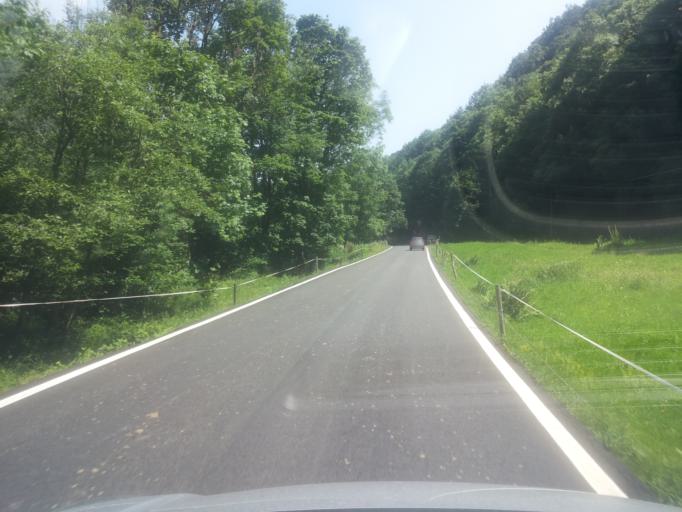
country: IT
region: Piedmont
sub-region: Provincia di Biella
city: Rosazza
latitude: 45.6817
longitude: 7.9706
